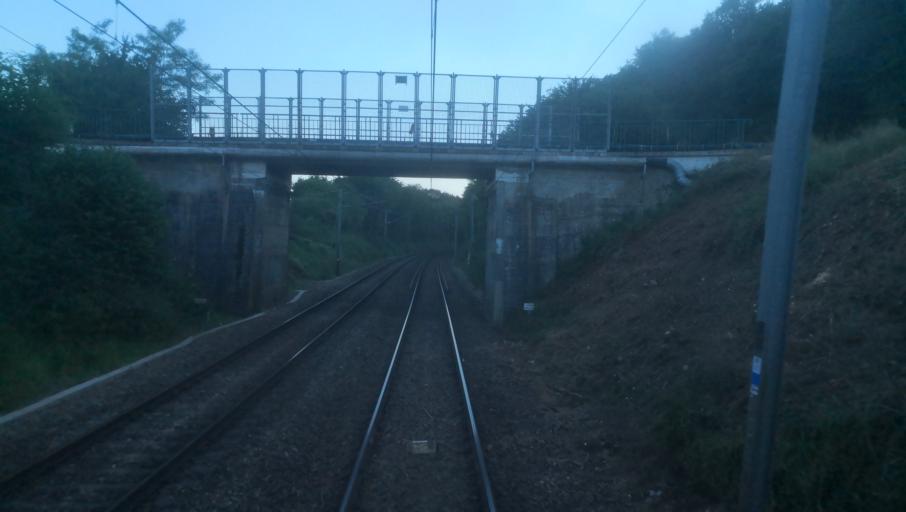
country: FR
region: Haute-Normandie
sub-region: Departement de l'Eure
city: Gravigny
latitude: 48.9923
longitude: 1.2365
